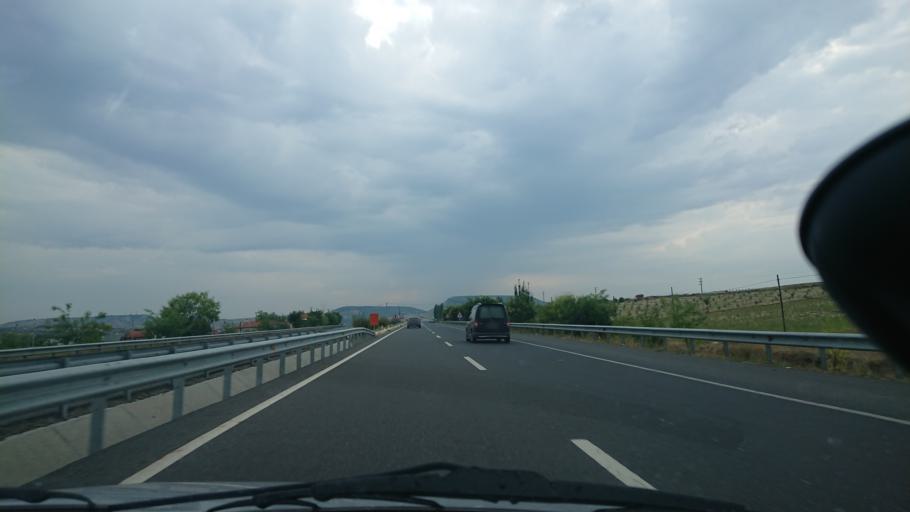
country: TR
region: Manisa
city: Selendi
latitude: 38.6194
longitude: 28.9046
